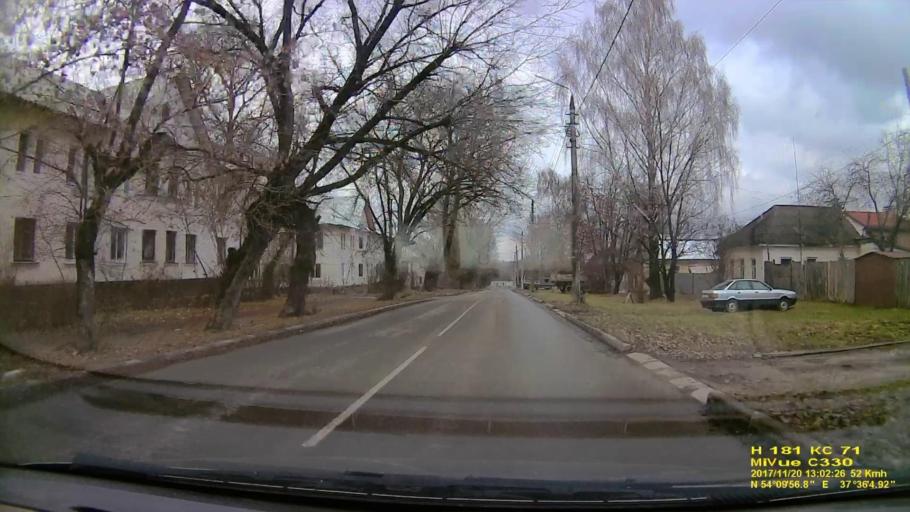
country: RU
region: Tula
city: Mendeleyevskiy
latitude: 54.1659
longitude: 37.6015
